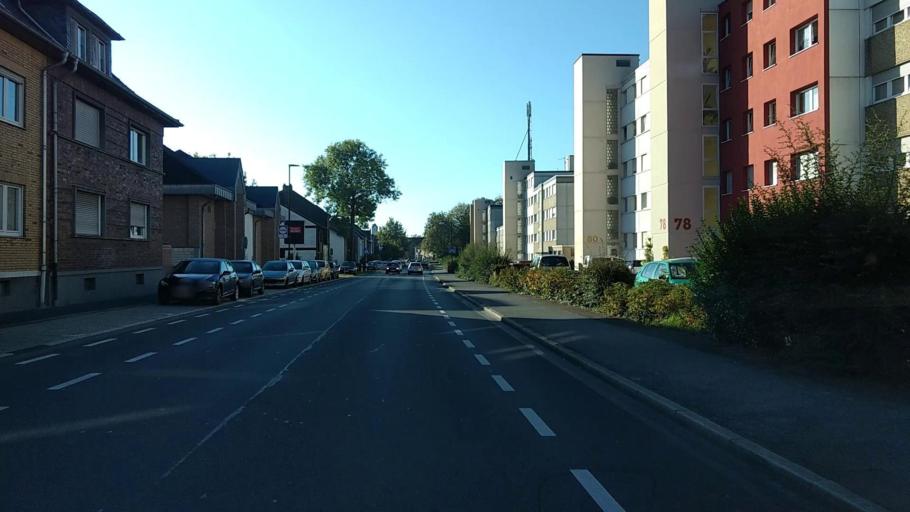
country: DE
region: North Rhine-Westphalia
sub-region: Regierungsbezirk Koln
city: Kerpen
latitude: 50.9219
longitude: 6.7069
